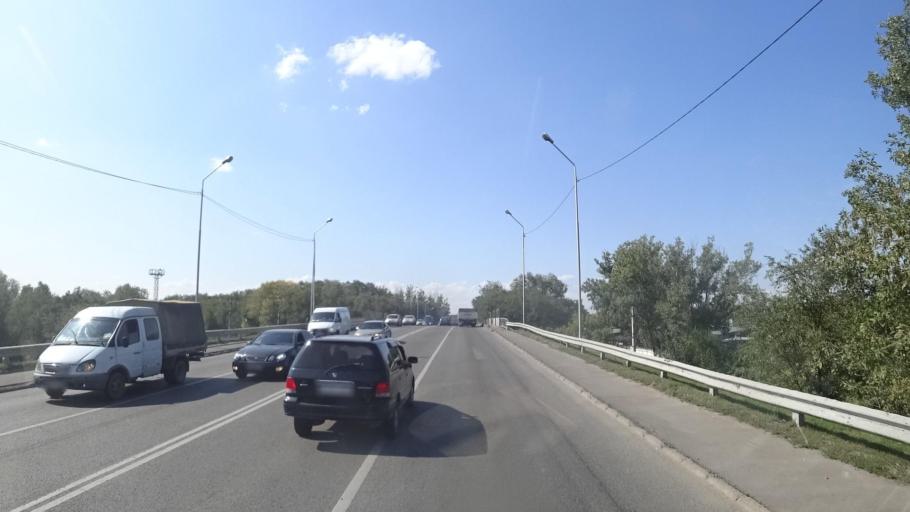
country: KZ
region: Almaty Oblysy
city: Pervomayskiy
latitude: 43.3422
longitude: 76.9789
